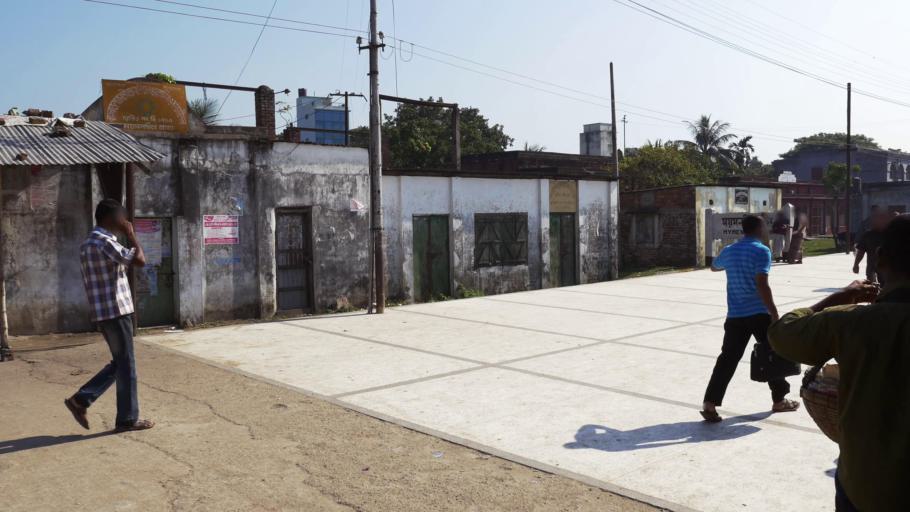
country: BD
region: Dhaka
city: Mymensingh
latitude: 24.7003
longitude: 90.4493
